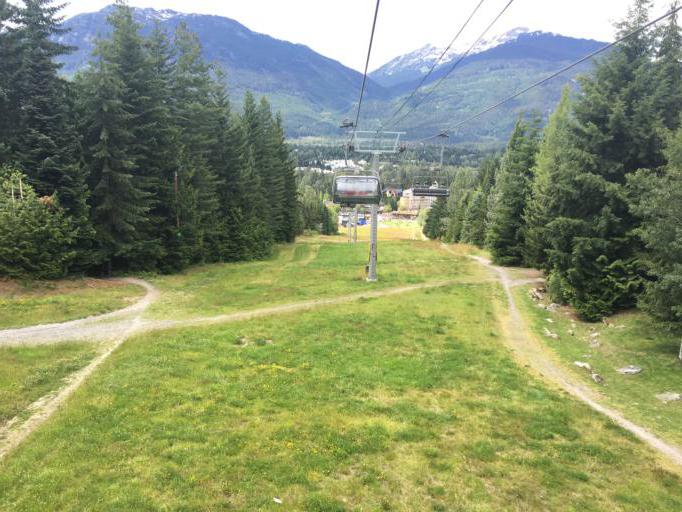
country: CA
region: British Columbia
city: Whistler
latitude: 50.1133
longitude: -122.9415
